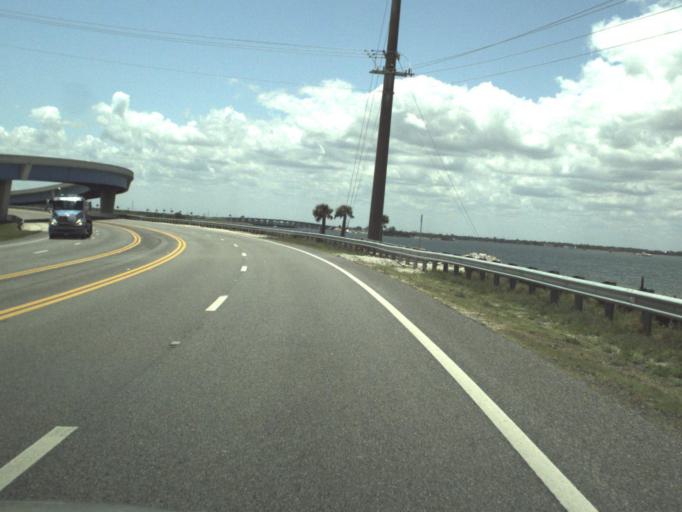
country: US
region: Florida
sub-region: Brevard County
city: Cape Canaveral
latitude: 28.4180
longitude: -80.6311
